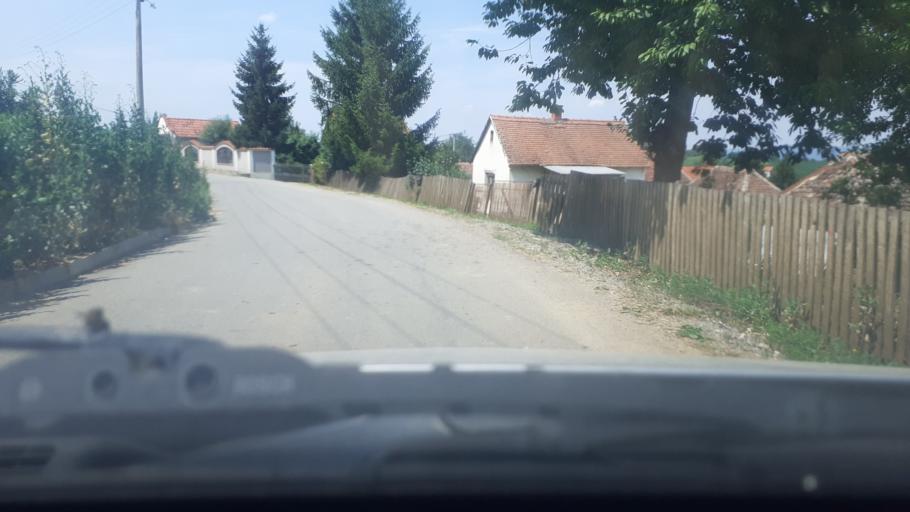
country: RS
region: Central Serbia
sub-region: Kolubarski Okrug
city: Osecina
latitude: 44.3914
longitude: 19.5003
